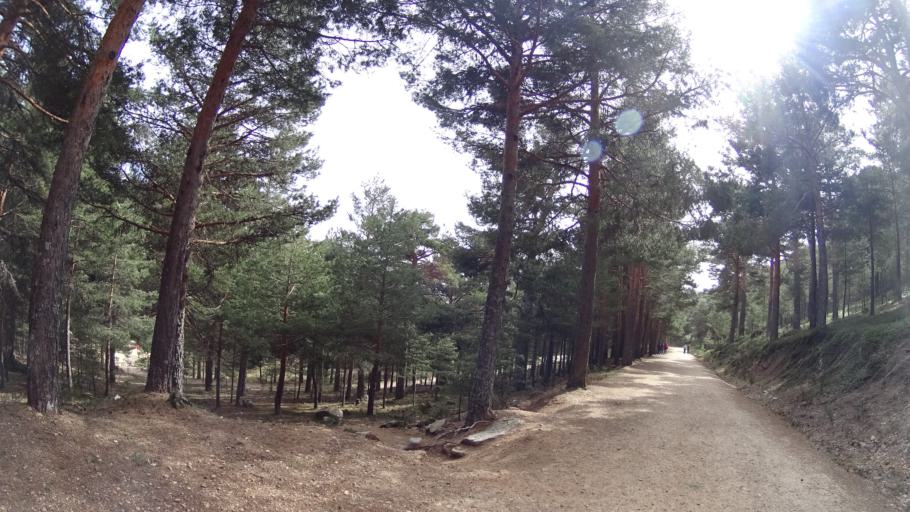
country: ES
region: Madrid
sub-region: Provincia de Madrid
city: Navacerrada
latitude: 40.7627
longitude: -3.9962
